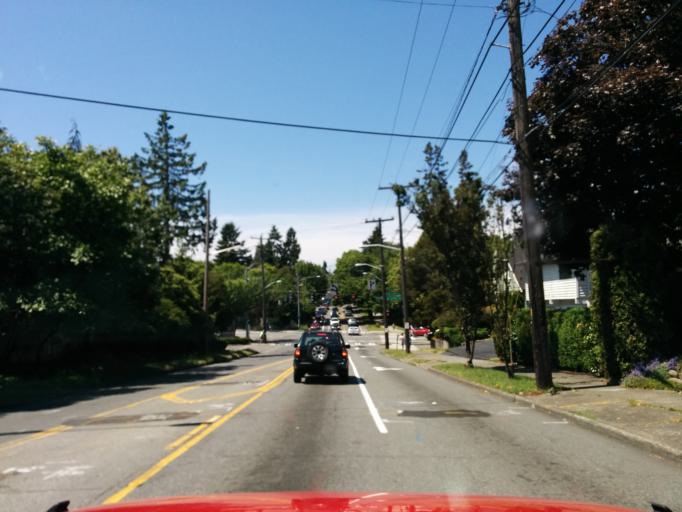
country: US
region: Washington
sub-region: King County
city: Seattle
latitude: 47.6651
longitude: -122.3391
